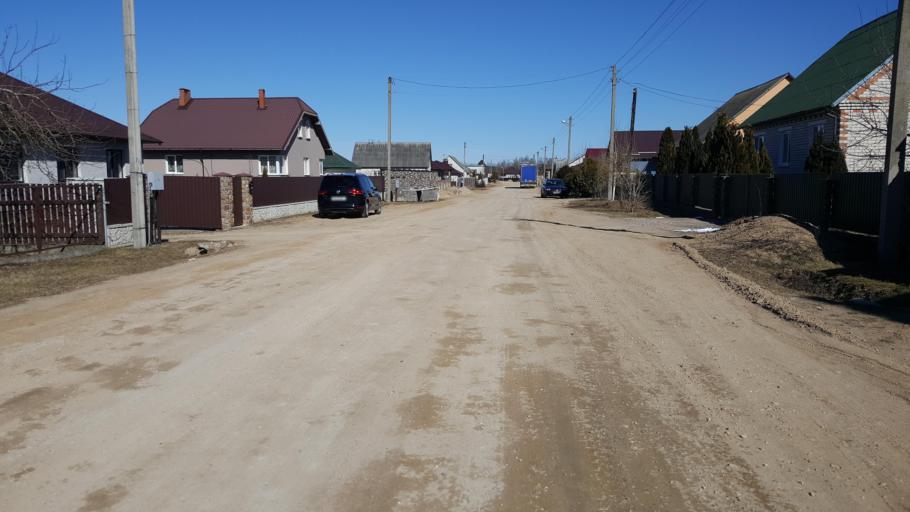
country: BY
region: Brest
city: Kamyanyets
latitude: 52.3986
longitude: 23.8412
